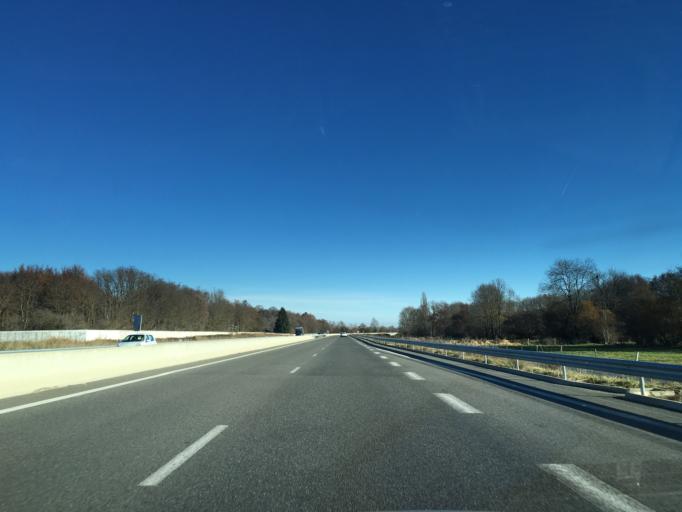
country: FR
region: Midi-Pyrenees
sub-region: Departement des Hautes-Pyrenees
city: Juillan
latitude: 43.1748
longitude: 0.0033
